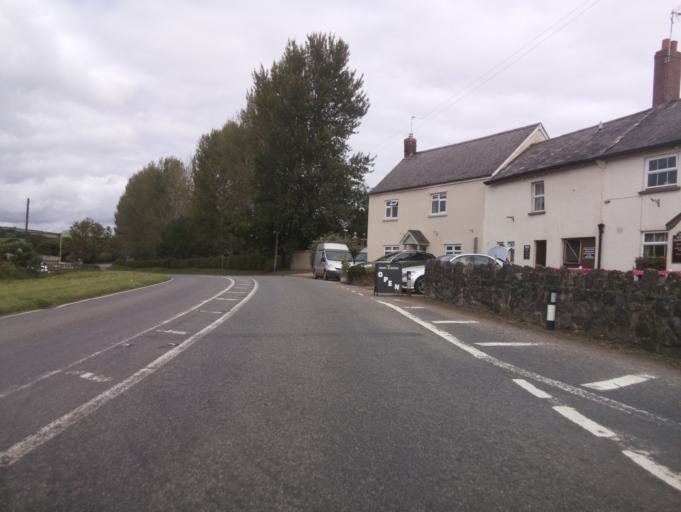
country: GB
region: England
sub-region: Devon
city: Bradninch
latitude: 50.8277
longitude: -3.3933
